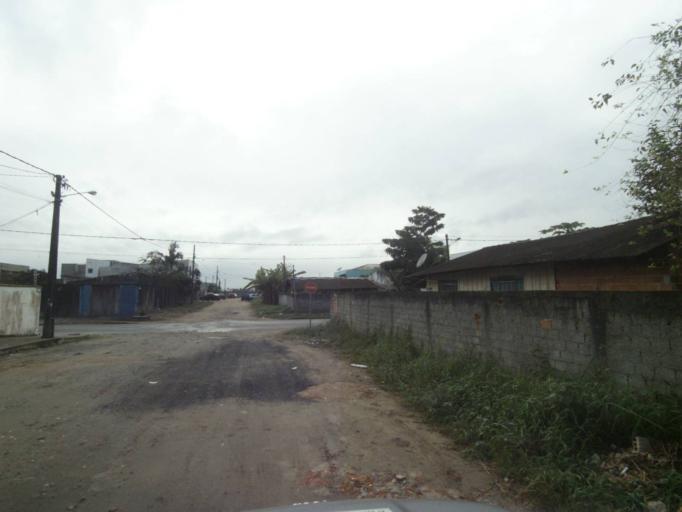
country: BR
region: Parana
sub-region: Paranagua
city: Paranagua
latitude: -25.5626
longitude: -48.5650
